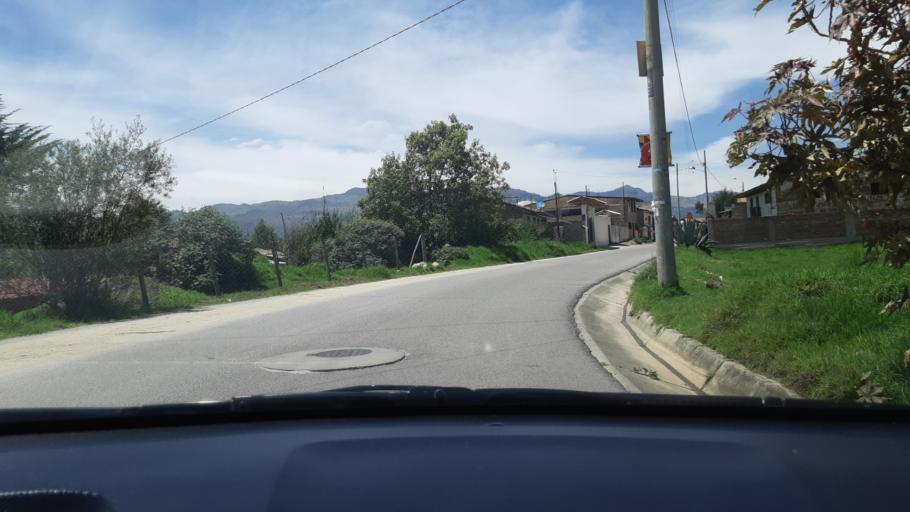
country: PE
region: Cajamarca
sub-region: Provincia de Cajamarca
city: Llacanora
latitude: -7.1831
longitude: -78.4473
